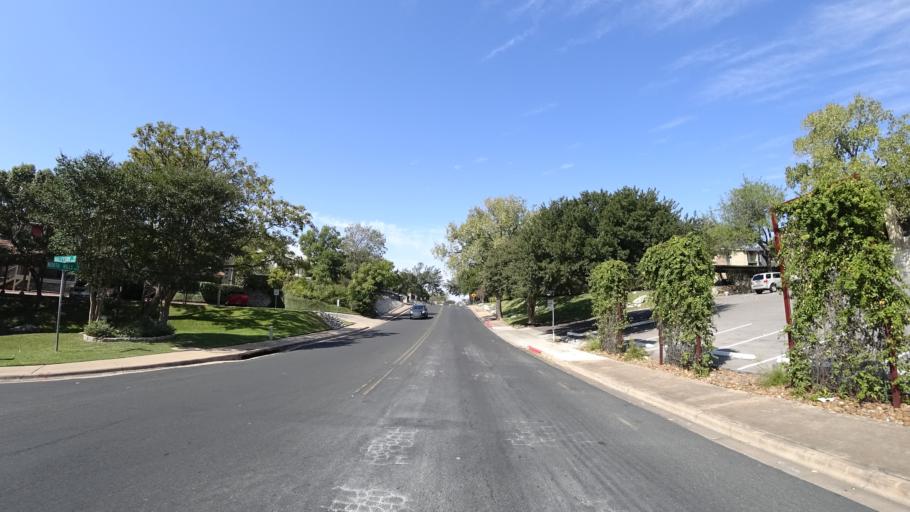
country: US
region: Texas
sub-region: Travis County
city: West Lake Hills
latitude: 30.3490
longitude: -97.7539
